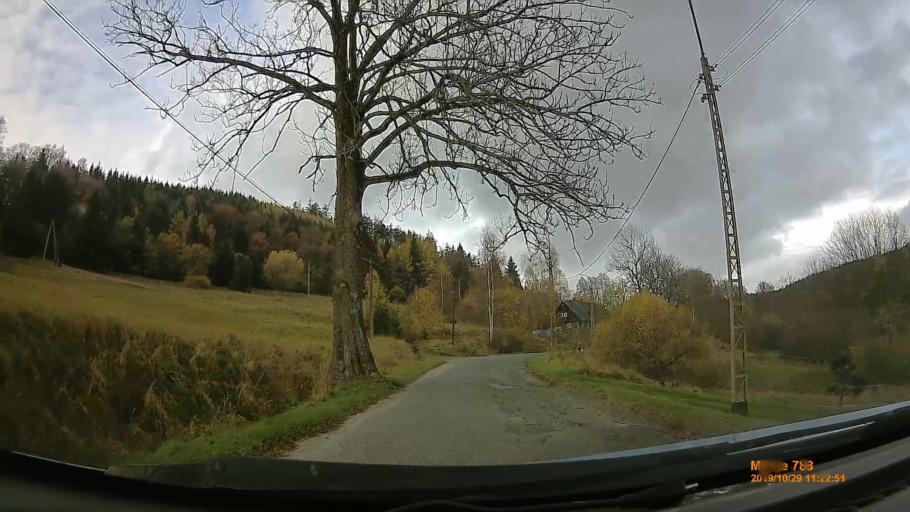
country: PL
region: Lower Silesian Voivodeship
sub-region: Powiat klodzki
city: Szczytna
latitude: 50.4356
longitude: 16.4285
